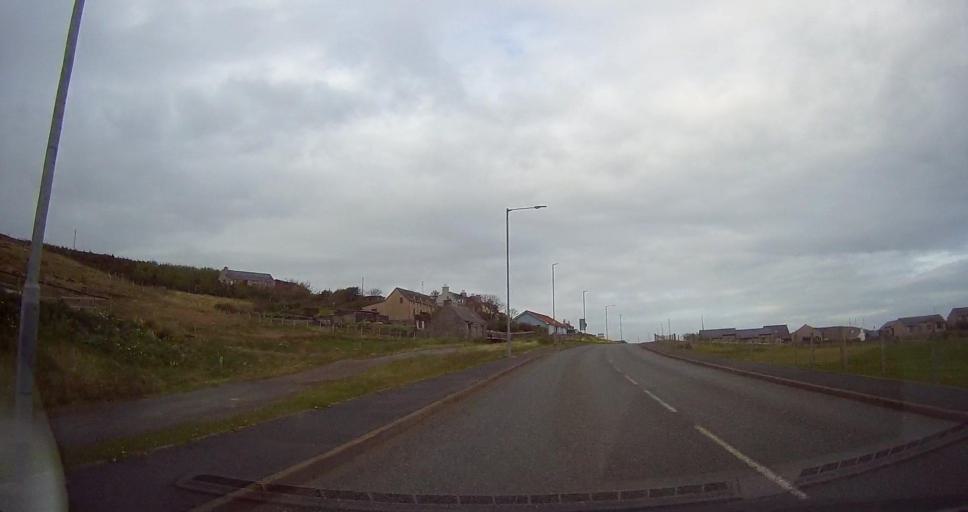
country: GB
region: Scotland
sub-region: Shetland Islands
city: Sandwick
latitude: 60.0434
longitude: -1.2292
